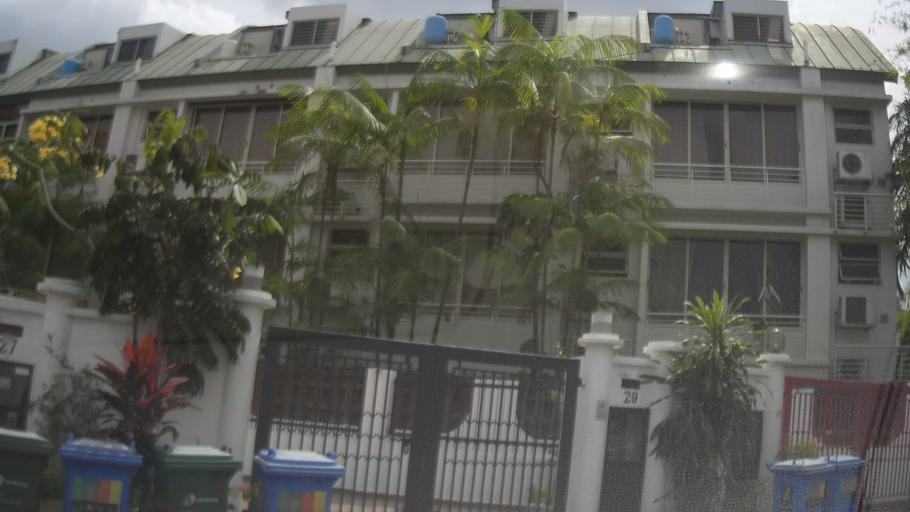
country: SG
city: Singapore
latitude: 1.3497
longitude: 103.8842
